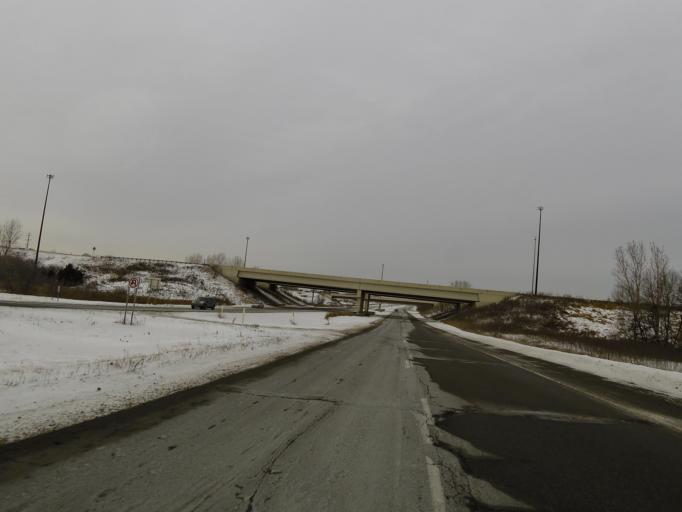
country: US
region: Minnesota
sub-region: Scott County
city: Savage
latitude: 44.7885
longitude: -93.4046
